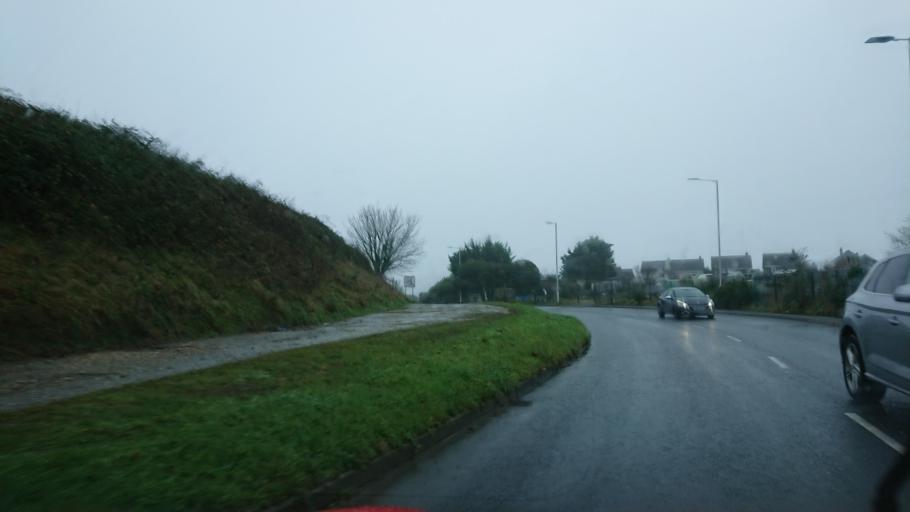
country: GB
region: England
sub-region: Plymouth
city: Plymstock
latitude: 50.3553
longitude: -4.1174
